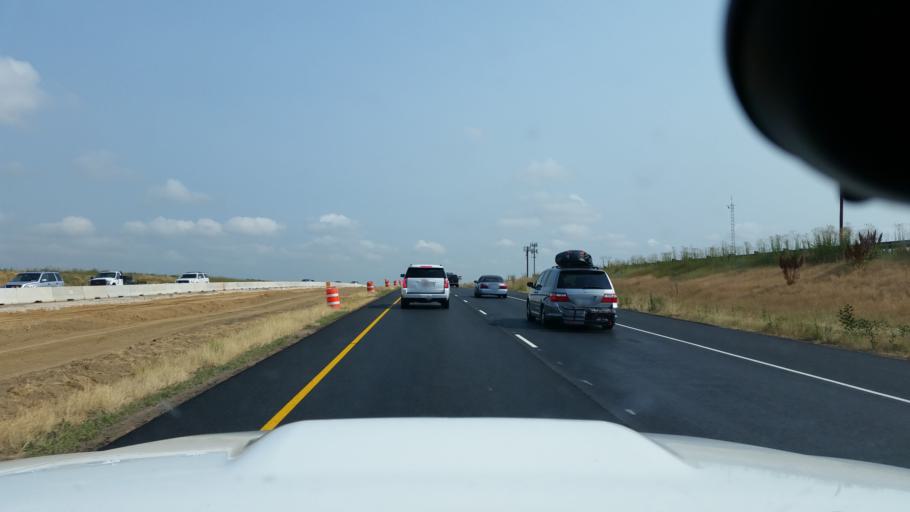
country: US
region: Colorado
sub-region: Weld County
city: Mead
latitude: 40.2676
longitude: -104.9801
